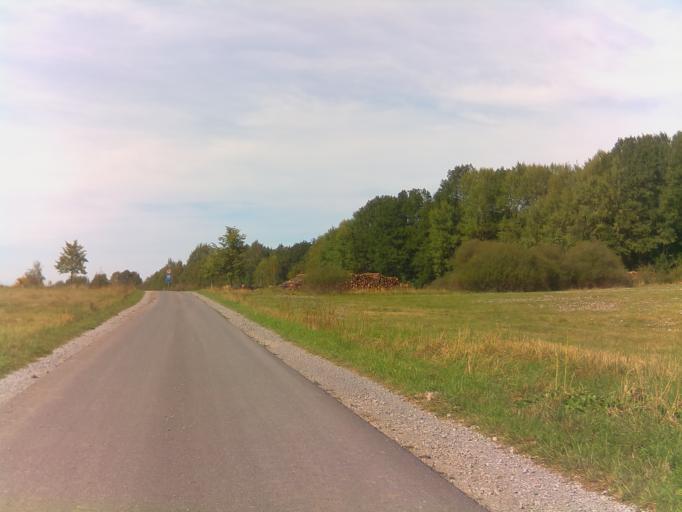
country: DE
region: Thuringia
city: Metzels
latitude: 50.6420
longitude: 10.4617
